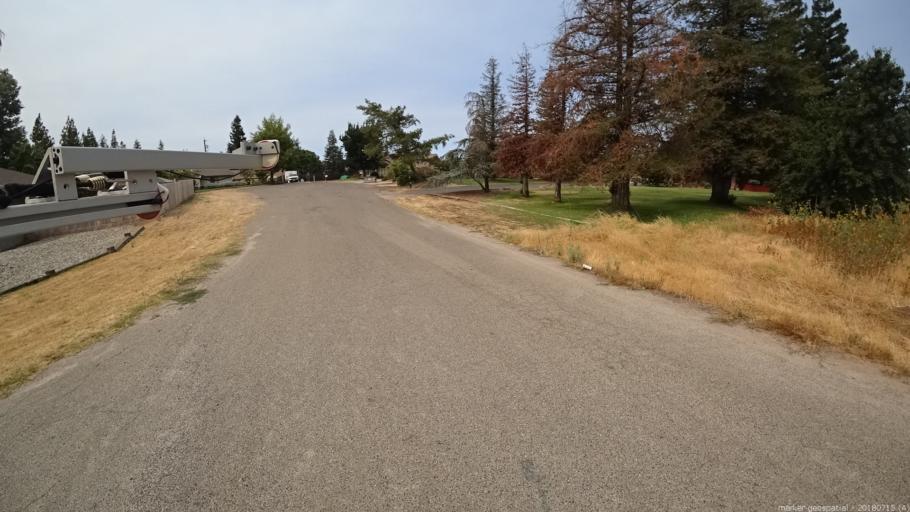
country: US
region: California
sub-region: Madera County
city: Madera Acres
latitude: 37.0196
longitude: -120.0668
